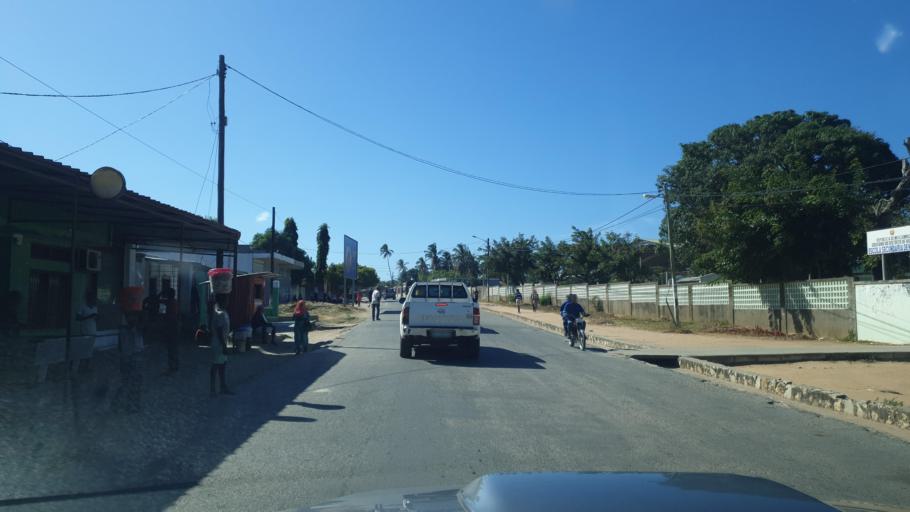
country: MZ
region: Nampula
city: Nacala
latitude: -14.5388
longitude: 40.6844
